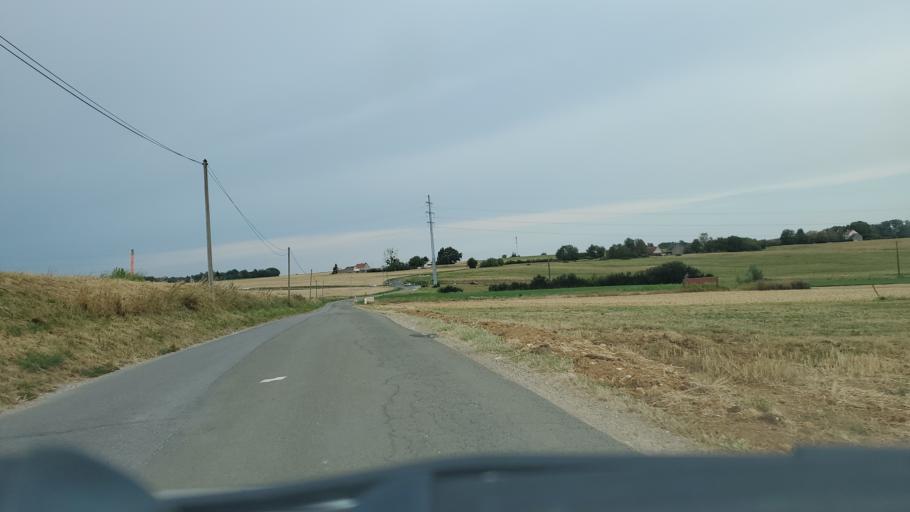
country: FR
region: Ile-de-France
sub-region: Departement de Seine-et-Marne
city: Chailly-en-Brie
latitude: 48.7788
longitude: 3.1632
